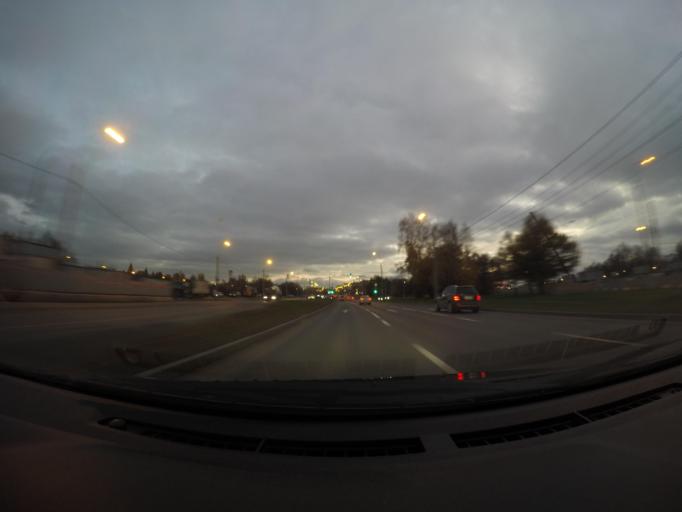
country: RU
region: Moscow
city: Kolomenskoye
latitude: 55.6588
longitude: 37.6539
